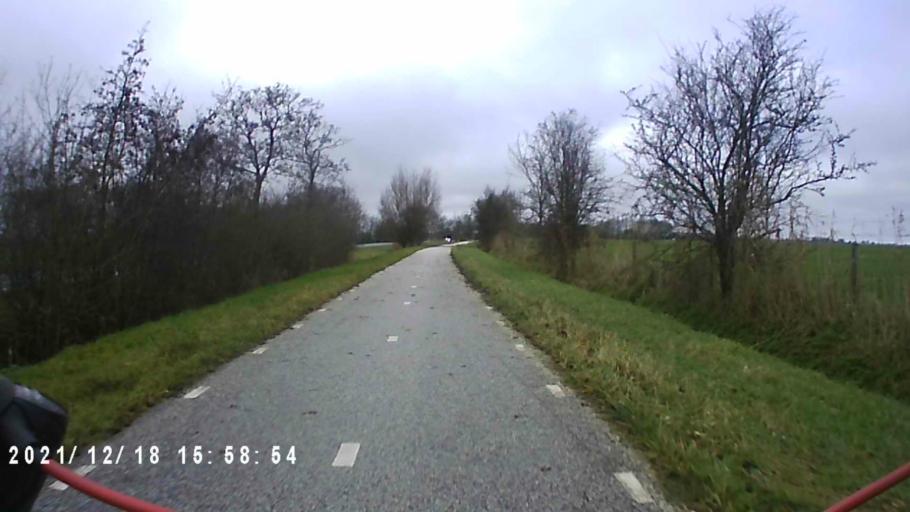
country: NL
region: Friesland
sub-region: Gemeente Dongeradeel
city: Anjum
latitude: 53.3381
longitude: 6.0914
